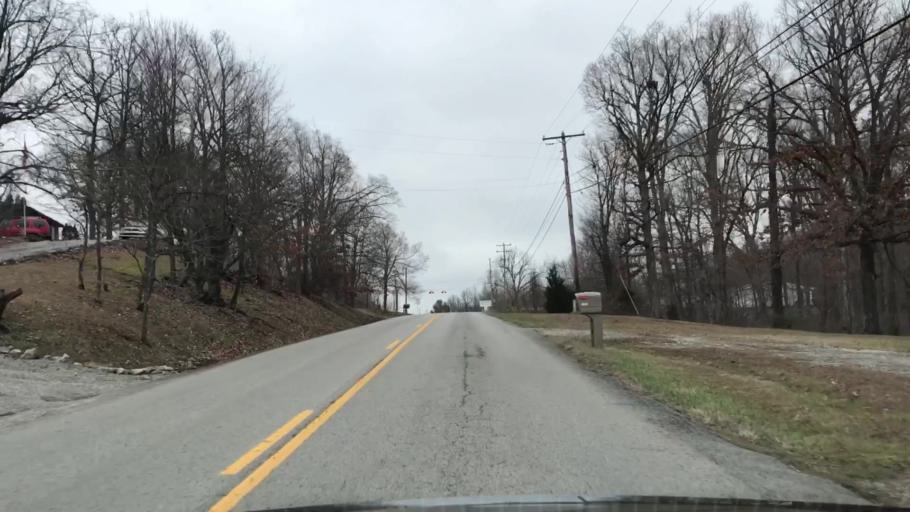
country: US
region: Kentucky
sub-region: Muhlenberg County
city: Morehead
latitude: 37.2405
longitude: -87.1939
